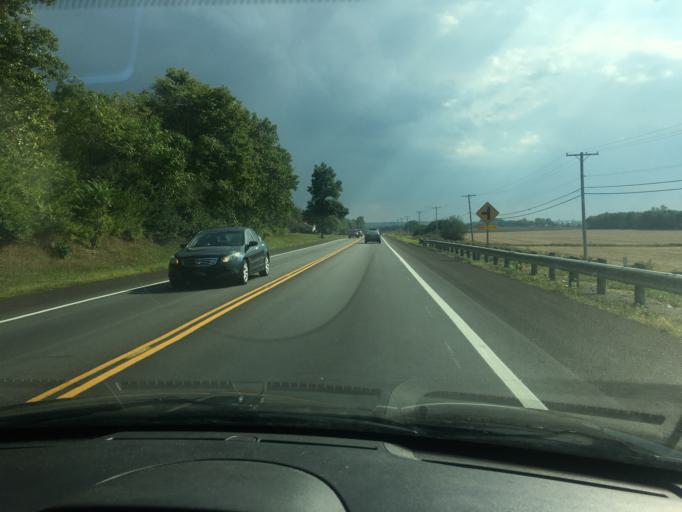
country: US
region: Ohio
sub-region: Champaign County
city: Urbana
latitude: 40.0620
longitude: -83.7775
